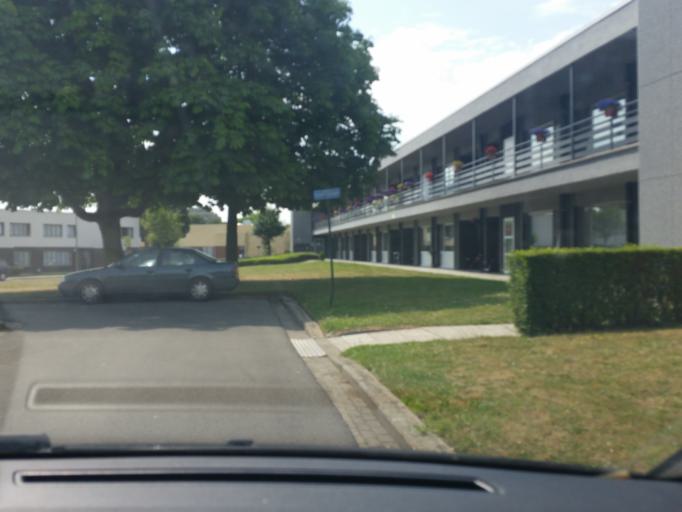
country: BE
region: Flanders
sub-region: Provincie Antwerpen
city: Mechelen
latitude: 51.0020
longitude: 4.4840
